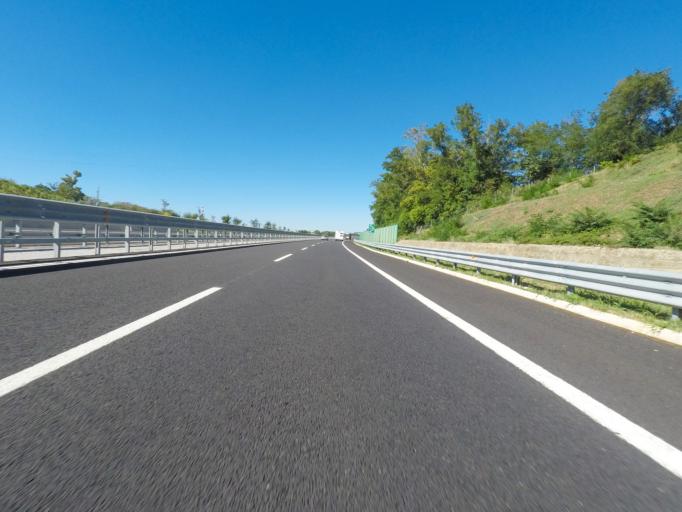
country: IT
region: Latium
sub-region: Provincia di Viterbo
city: Tarquinia
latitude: 42.2470
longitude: 11.7379
